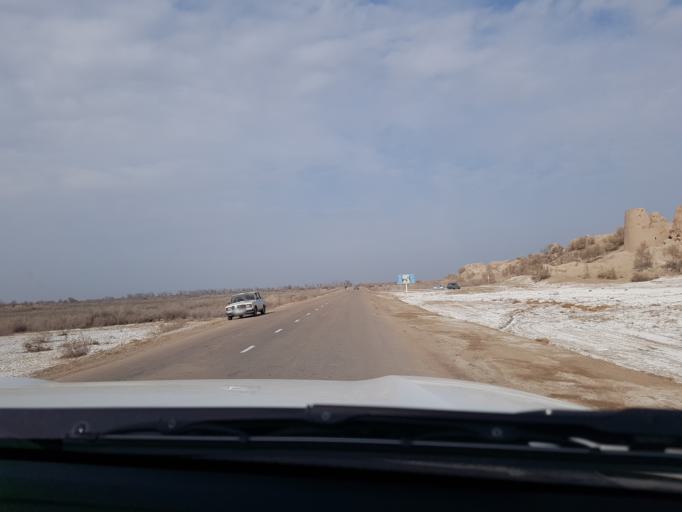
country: TM
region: Dasoguz
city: Yylanly
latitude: 41.7279
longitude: 59.7193
